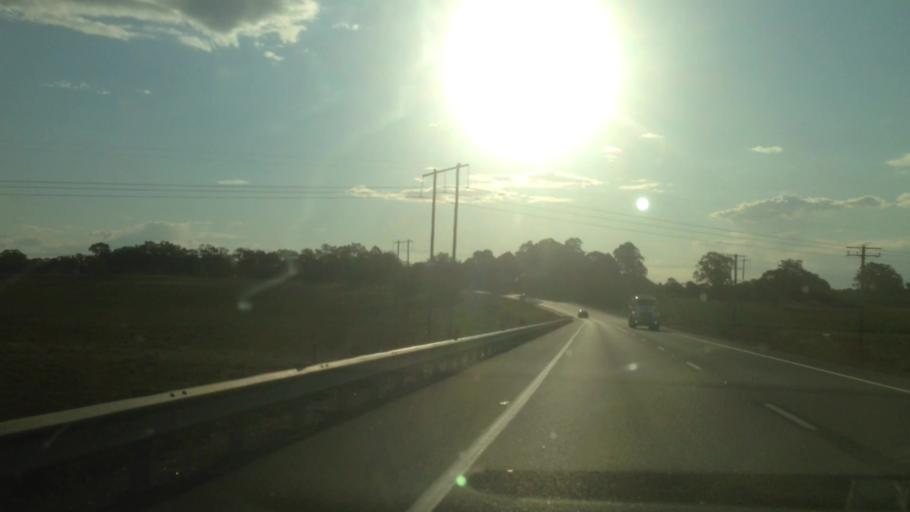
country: AU
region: New South Wales
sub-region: Cessnock
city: Heddon Greta
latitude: -32.8309
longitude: 151.5192
